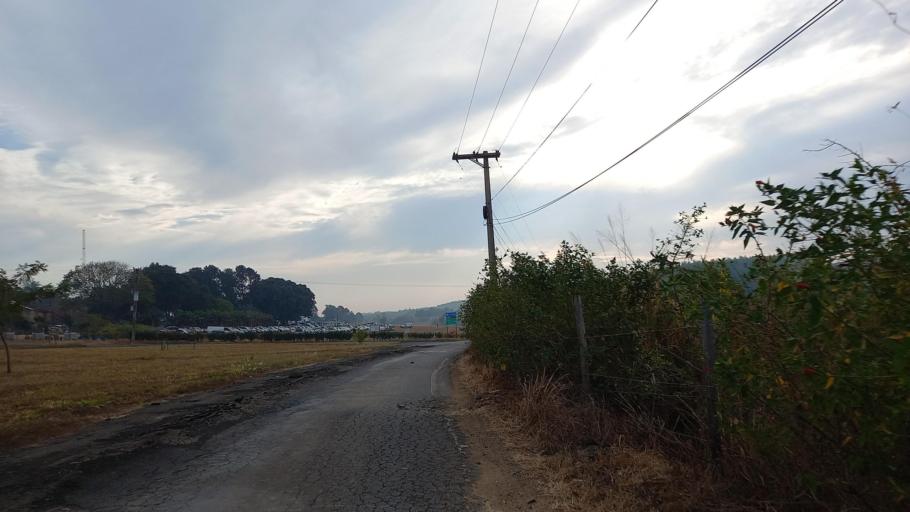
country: BR
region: Sao Paulo
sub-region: Moji-Guacu
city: Mogi-Gaucu
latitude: -22.3326
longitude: -46.8808
